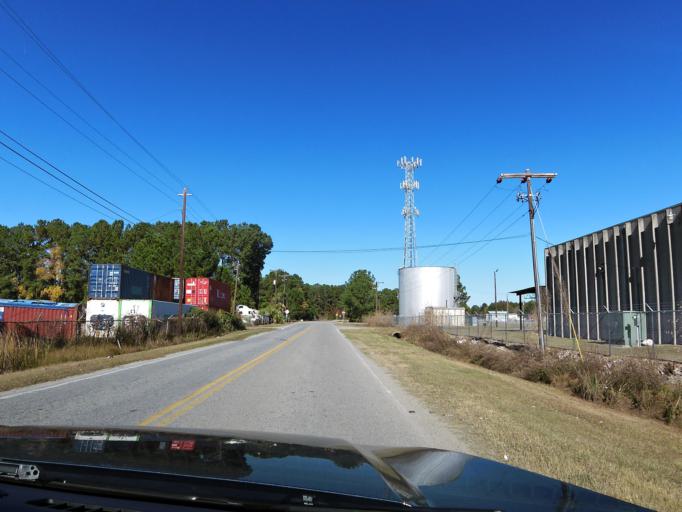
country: US
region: Georgia
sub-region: Chatham County
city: Savannah
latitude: 32.0673
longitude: -81.1433
